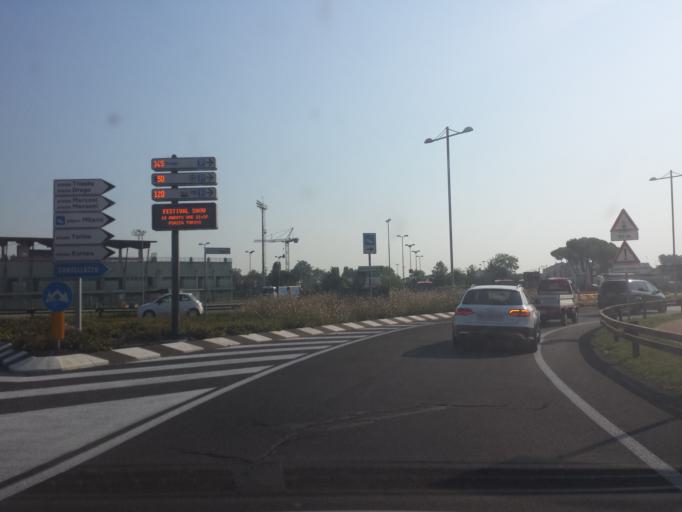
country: IT
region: Veneto
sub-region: Provincia di Venezia
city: Lido di Iesolo
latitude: 45.5095
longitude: 12.6363
